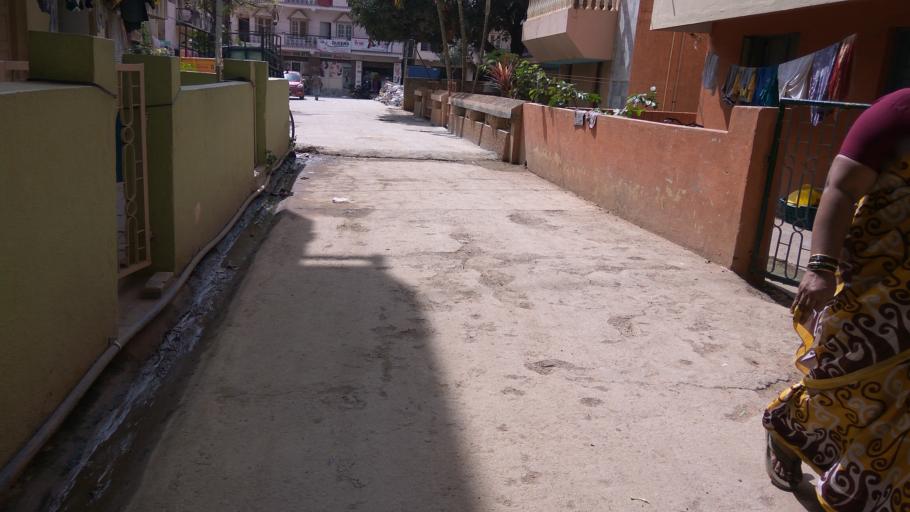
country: IN
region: Karnataka
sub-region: Bangalore Urban
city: Bangalore
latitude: 12.9551
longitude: 77.6934
